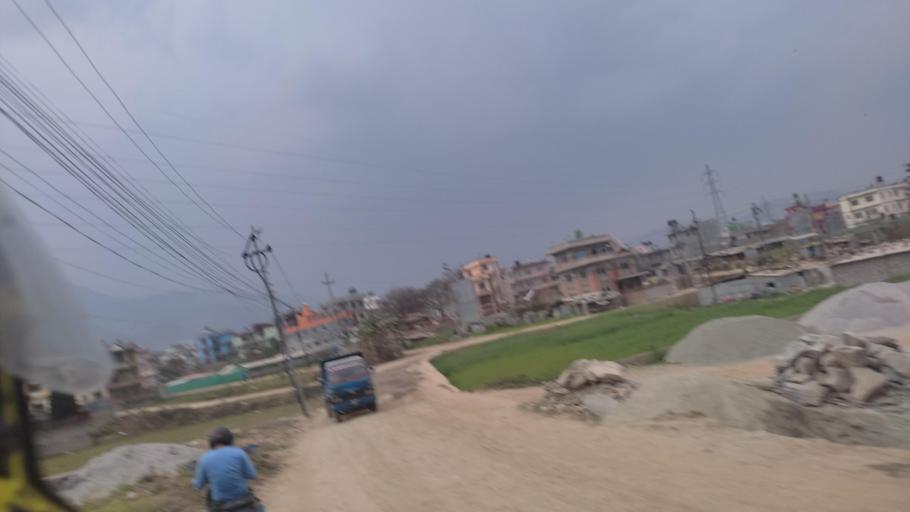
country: NP
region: Central Region
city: Kirtipur
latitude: 27.6650
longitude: 85.2705
